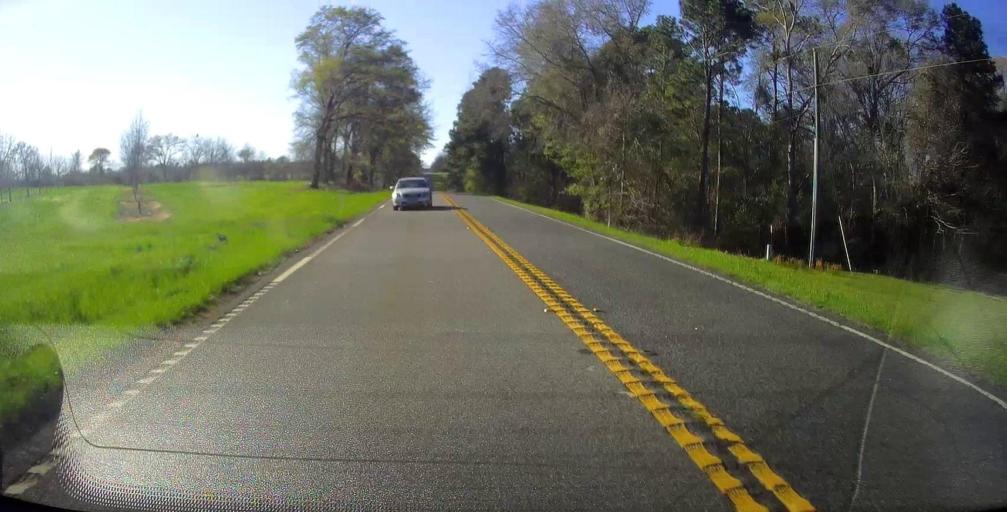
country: US
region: Georgia
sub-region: Macon County
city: Marshallville
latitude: 32.4421
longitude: -83.8919
